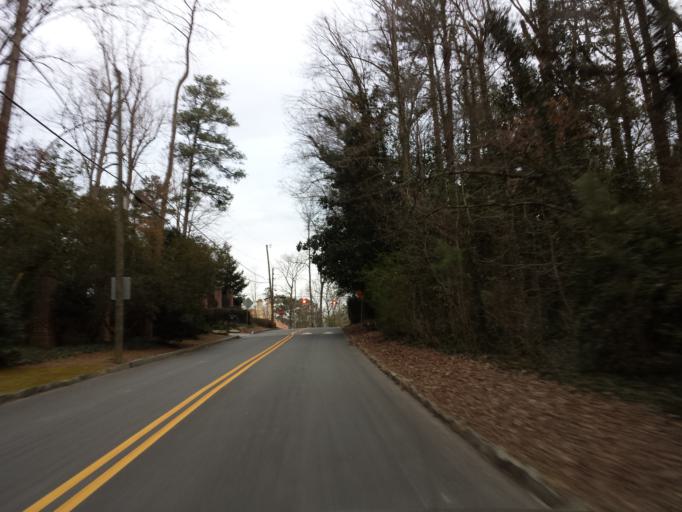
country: US
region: Georgia
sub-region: Cobb County
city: Vinings
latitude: 33.8832
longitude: -84.4183
